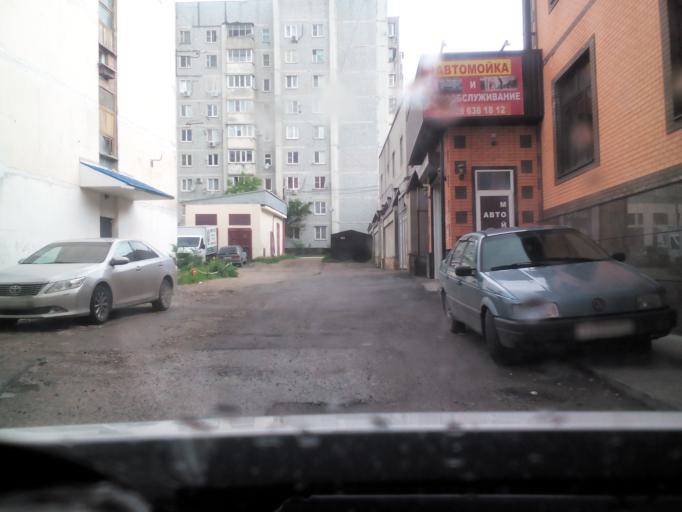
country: RU
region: Stavropol'skiy
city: Pyatigorsk
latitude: 44.0543
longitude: 43.0421
